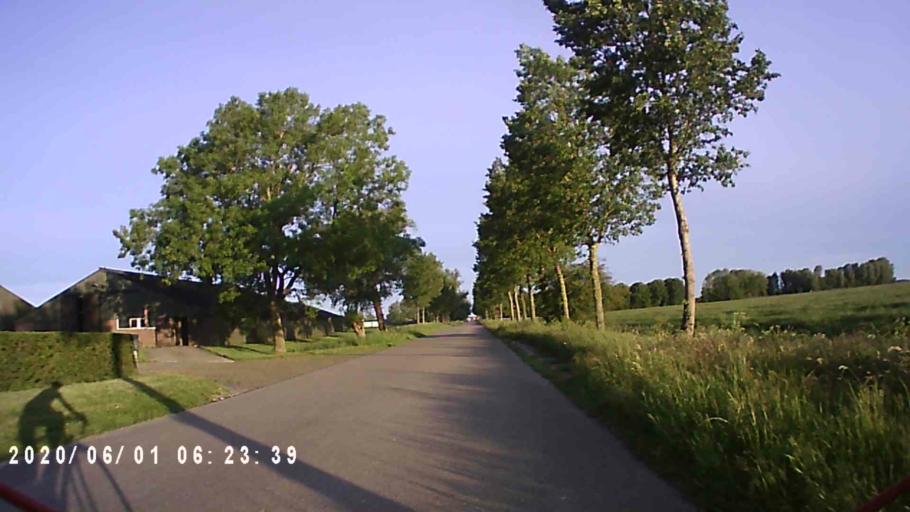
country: NL
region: Friesland
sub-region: Gemeente Kollumerland en Nieuwkruisland
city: Kollum
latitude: 53.2660
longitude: 6.2148
